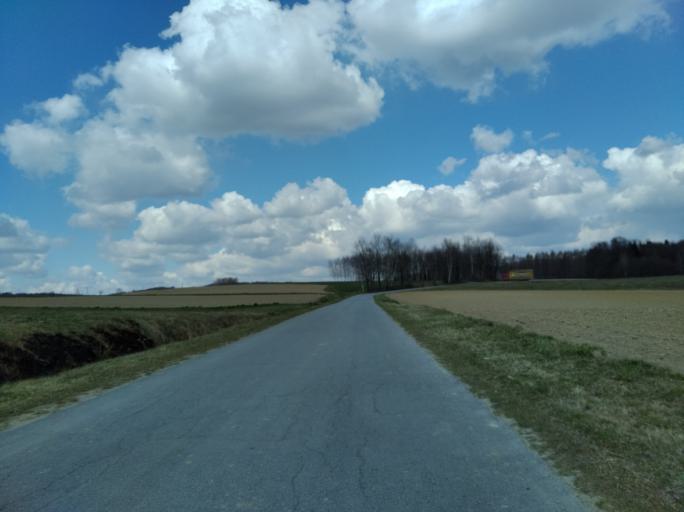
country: PL
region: Subcarpathian Voivodeship
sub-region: Powiat strzyzowski
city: Wisniowa
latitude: 49.9169
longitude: 21.7045
